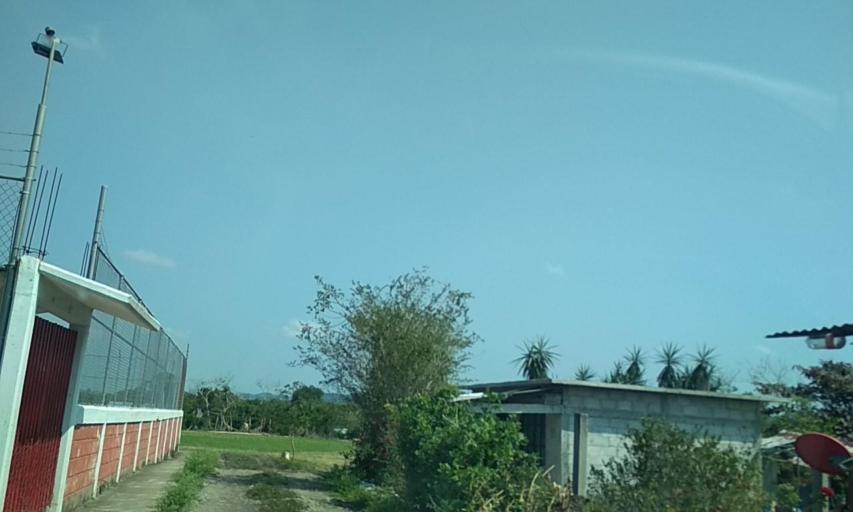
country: MX
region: Veracruz
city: Gutierrez Zamora
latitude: 20.3765
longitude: -97.1488
